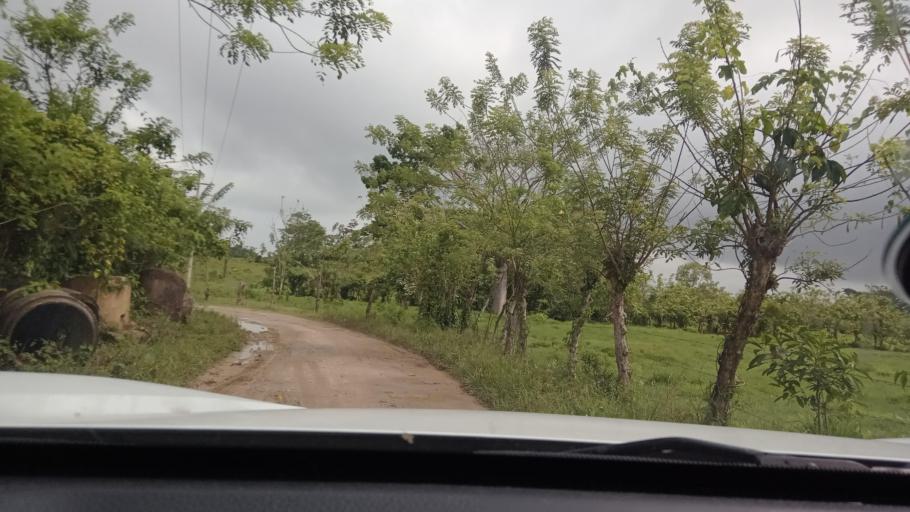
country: MX
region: Tabasco
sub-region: Huimanguillo
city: Francisco Rueda
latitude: 17.5161
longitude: -94.1195
